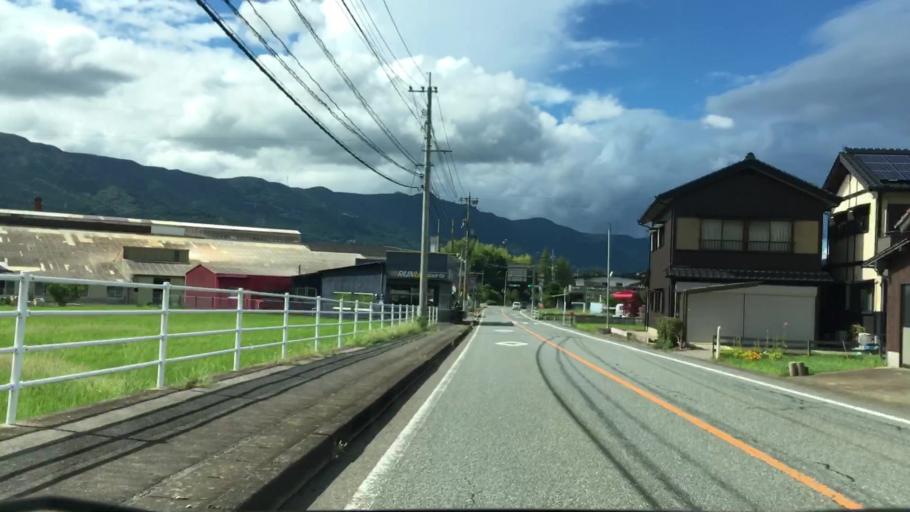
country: JP
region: Saga Prefecture
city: Imaricho-ko
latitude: 33.1861
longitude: 129.8536
